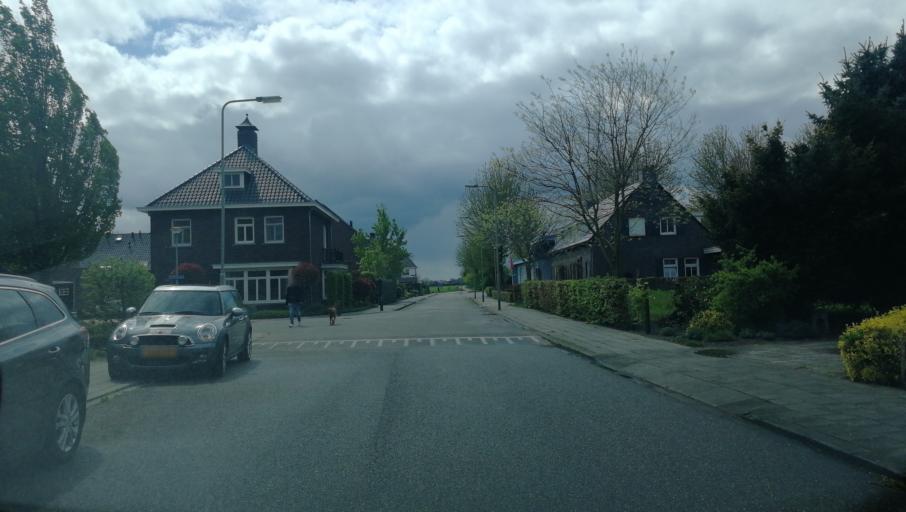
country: NL
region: Limburg
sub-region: Gemeente Peel en Maas
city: Maasbree
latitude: 51.4071
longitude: 6.0324
